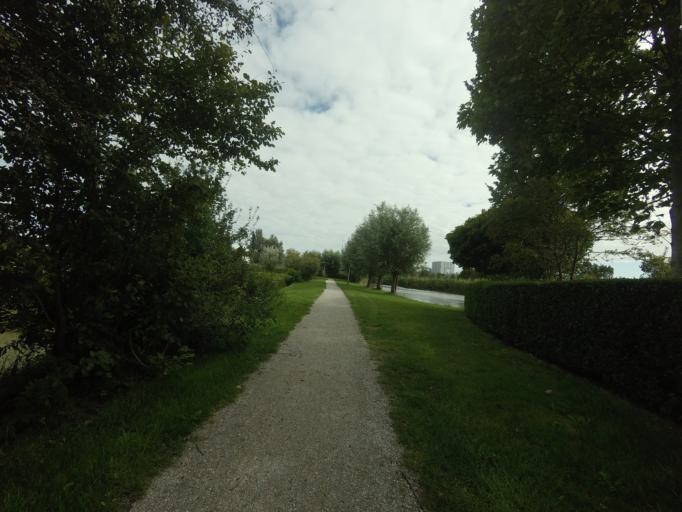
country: NL
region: Friesland
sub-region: Sudwest Fryslan
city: Workum
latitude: 52.9781
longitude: 5.4539
